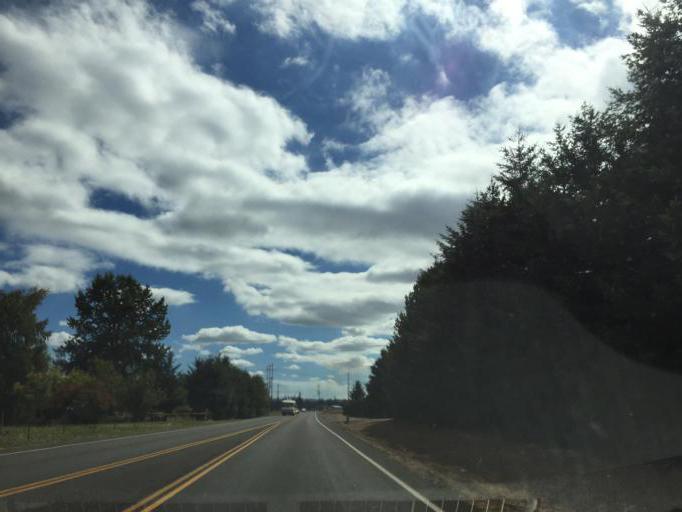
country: US
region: Oregon
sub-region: Marion County
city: Mount Angel
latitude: 45.1112
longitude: -122.7865
